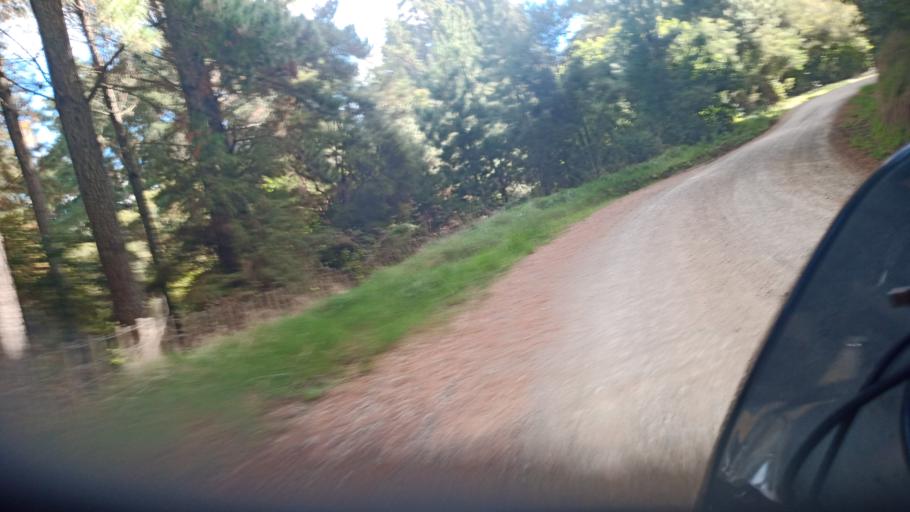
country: NZ
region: Gisborne
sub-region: Gisborne District
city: Gisborne
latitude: -38.4217
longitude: 177.7067
